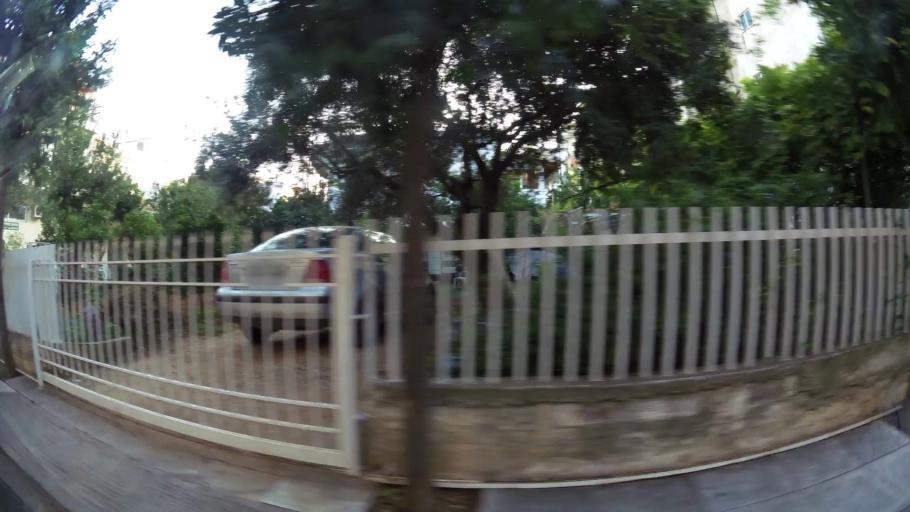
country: GR
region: Attica
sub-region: Nomarchia Athinas
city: Agia Paraskevi
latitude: 38.0200
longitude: 23.8329
